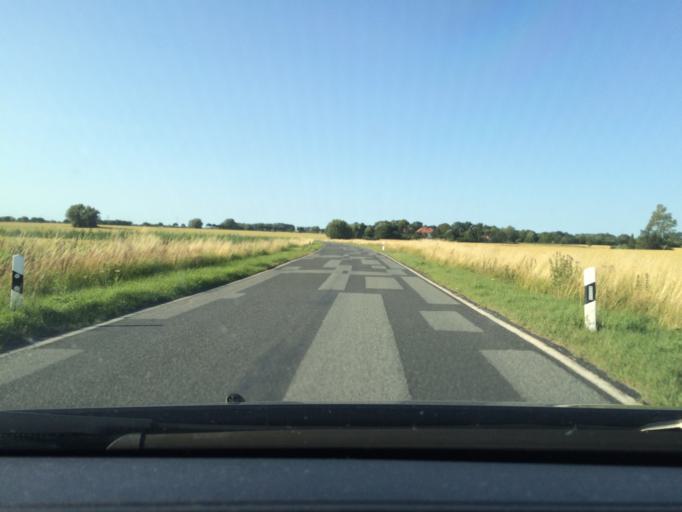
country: DE
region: Mecklenburg-Vorpommern
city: Altenpleen
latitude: 54.3796
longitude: 12.9418
